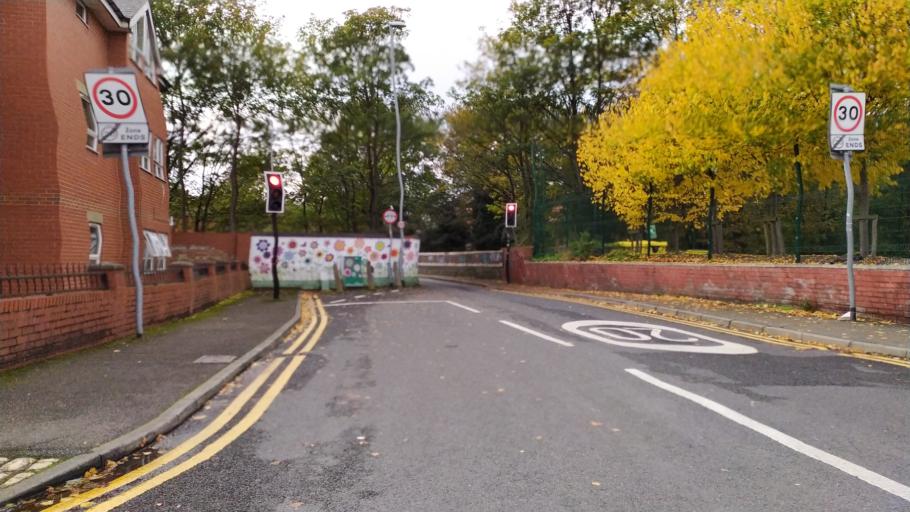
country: GB
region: England
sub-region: City and Borough of Leeds
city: Leeds
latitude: 53.8152
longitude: -1.5831
